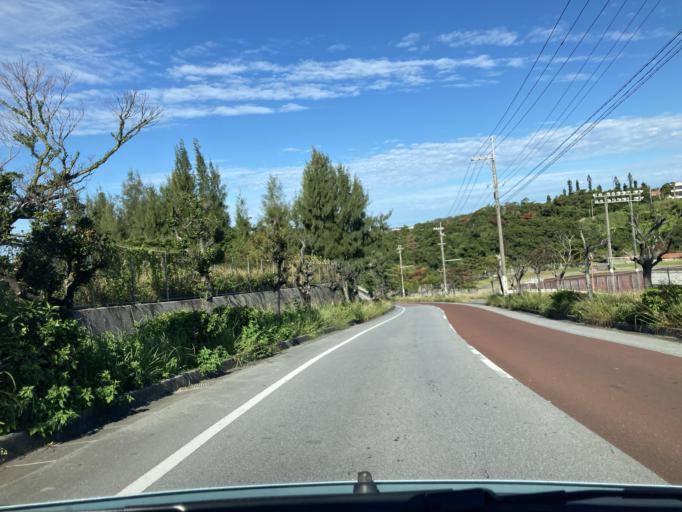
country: JP
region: Okinawa
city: Okinawa
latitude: 26.3690
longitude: 127.7715
